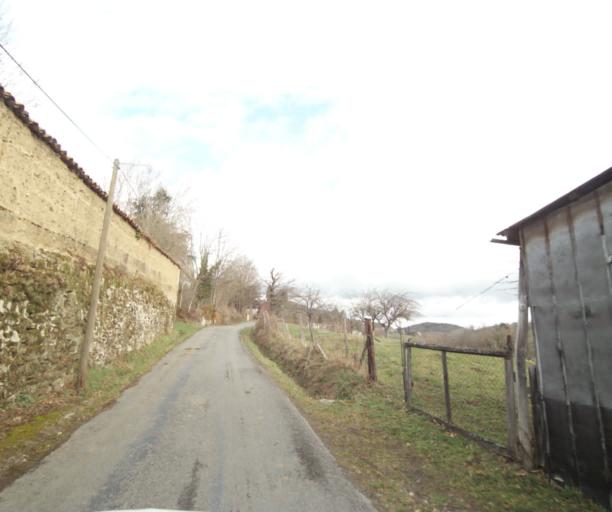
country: FR
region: Rhone-Alpes
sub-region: Departement de la Loire
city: La Talaudiere
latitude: 45.4813
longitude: 4.4111
